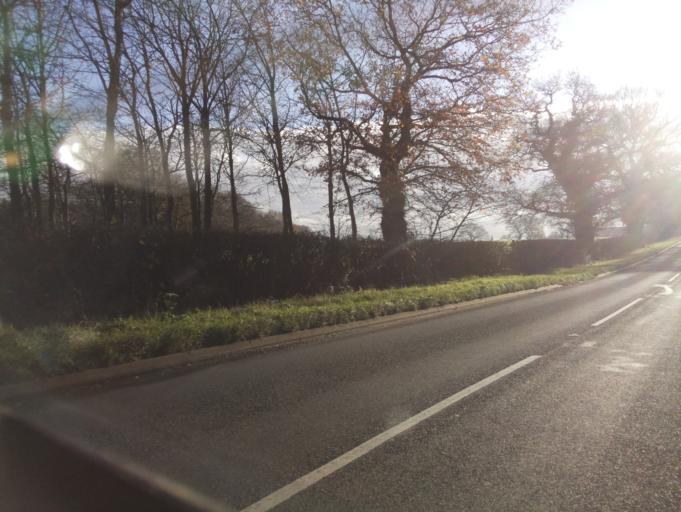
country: GB
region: England
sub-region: Staffordshire
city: Barton under Needwood
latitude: 52.8111
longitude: -1.7364
